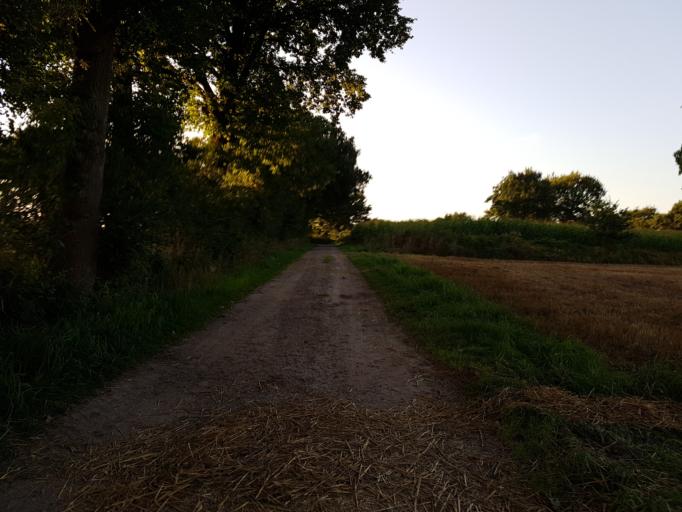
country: DE
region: Lower Saxony
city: Wittmund
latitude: 53.5383
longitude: 7.8240
